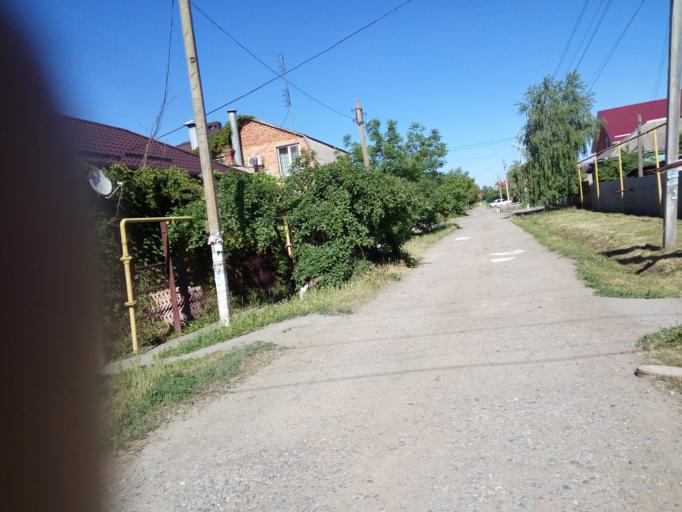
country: RU
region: Rostov
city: Bataysk
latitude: 47.1242
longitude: 39.7355
